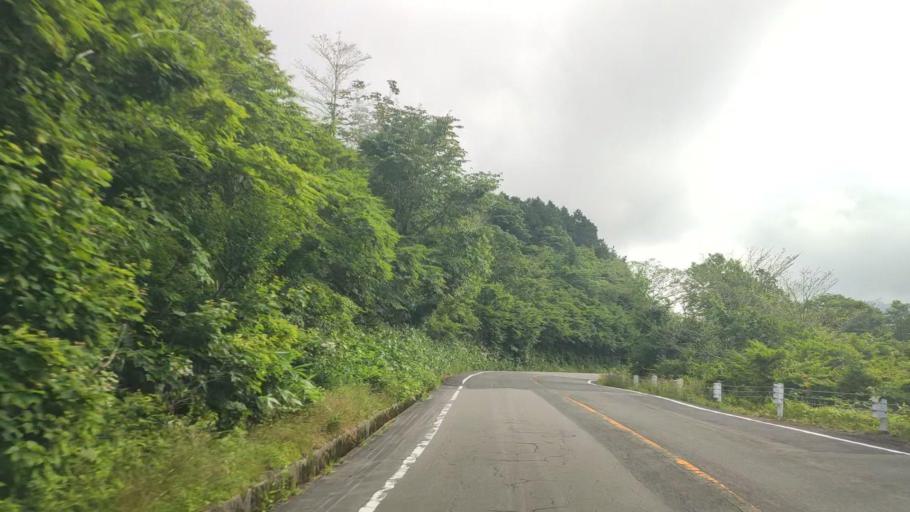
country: JP
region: Tottori
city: Kurayoshi
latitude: 35.3296
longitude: 133.5918
